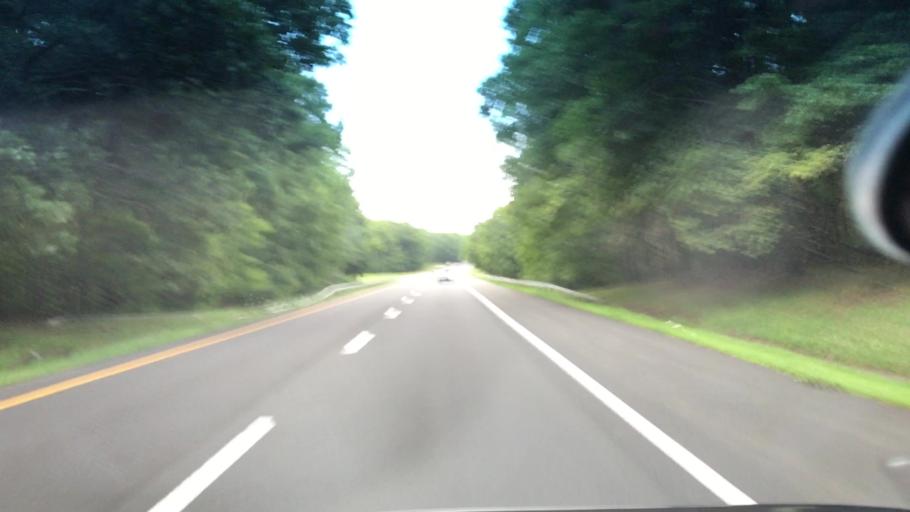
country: US
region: New York
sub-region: Suffolk County
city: East Shoreham
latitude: 40.9186
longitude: -72.8795
